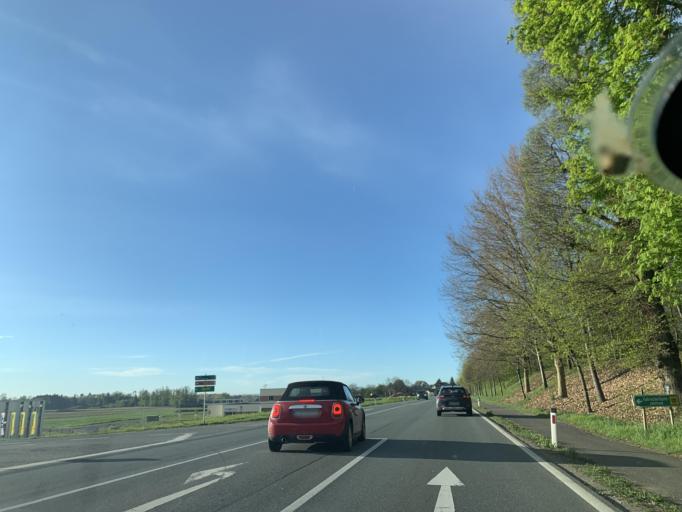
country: AT
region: Styria
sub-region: Politischer Bezirk Leibnitz
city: Lang
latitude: 46.8451
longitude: 15.5169
